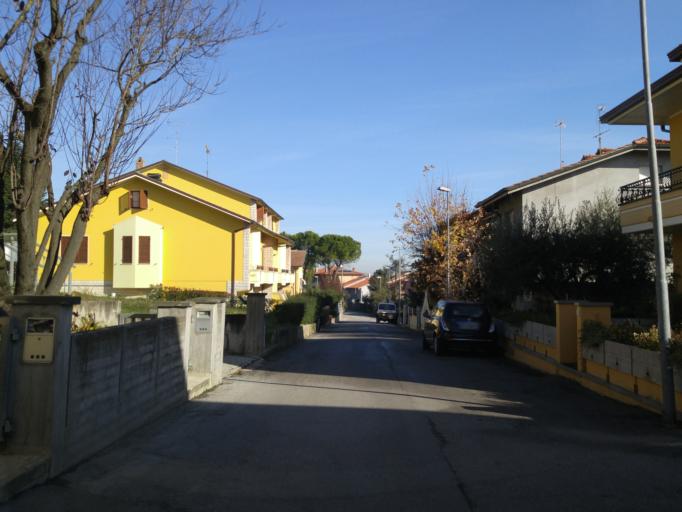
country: IT
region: The Marches
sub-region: Provincia di Pesaro e Urbino
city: Lucrezia
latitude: 43.7755
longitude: 12.9343
